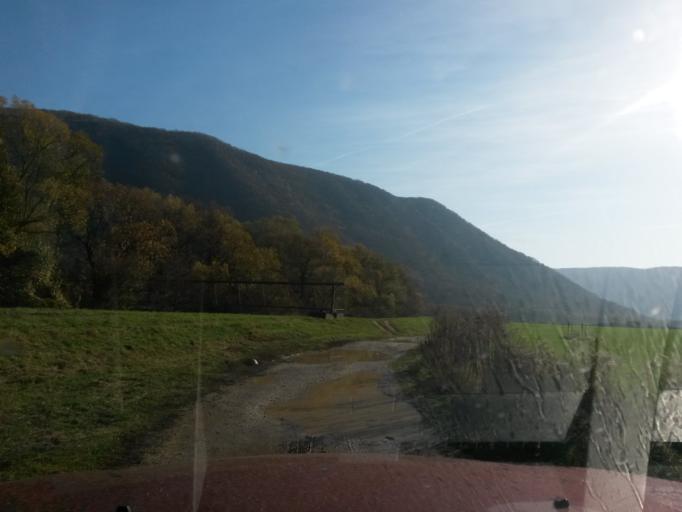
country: SK
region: Kosicky
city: Roznava
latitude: 48.5895
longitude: 20.4724
